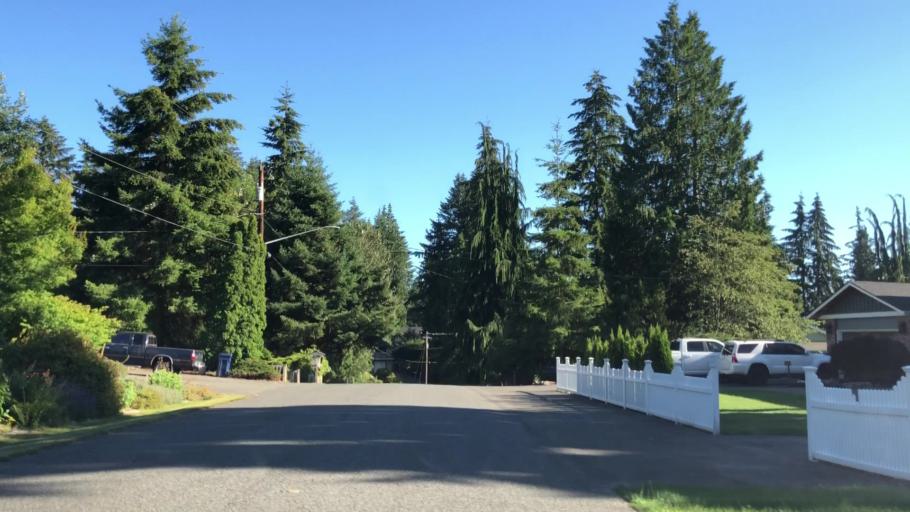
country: US
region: Washington
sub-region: Snohomish County
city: Martha Lake
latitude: 47.8432
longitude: -122.2558
